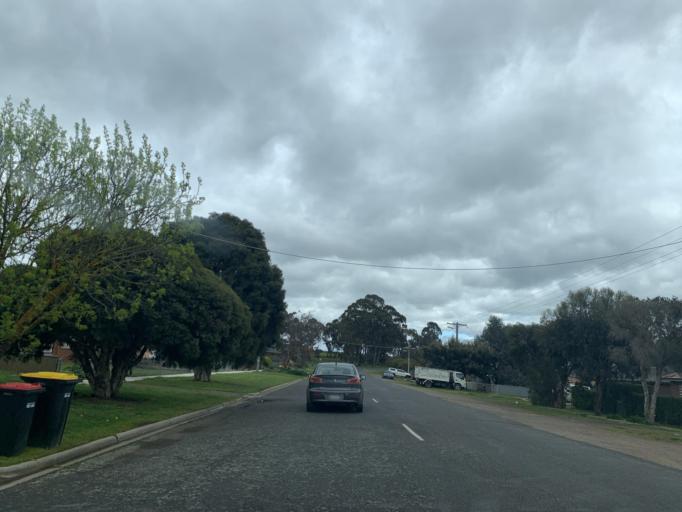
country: AU
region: Victoria
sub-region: Whittlesea
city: Whittlesea
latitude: -37.2102
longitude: 145.0424
